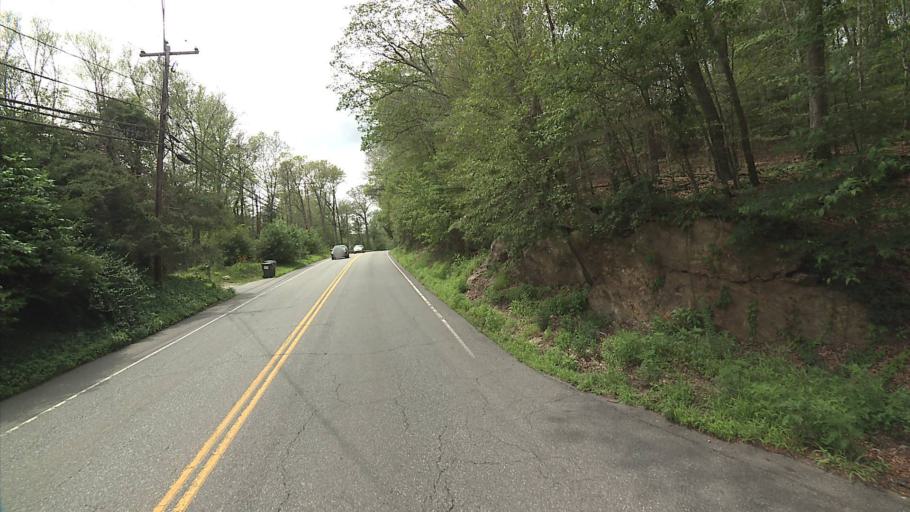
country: US
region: Connecticut
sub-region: Middlesex County
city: Deep River Center
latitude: 41.3808
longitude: -72.4505
